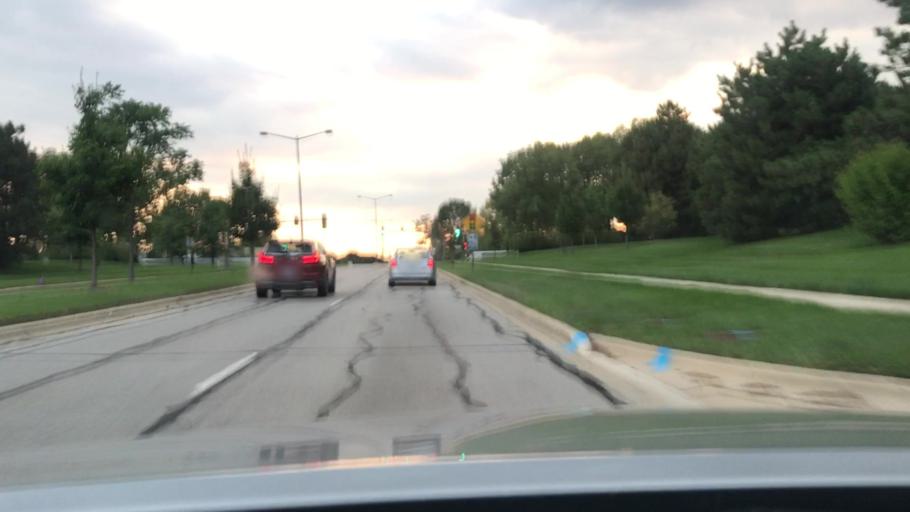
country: US
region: Illinois
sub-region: DuPage County
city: Warrenville
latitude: 41.7690
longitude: -88.2189
